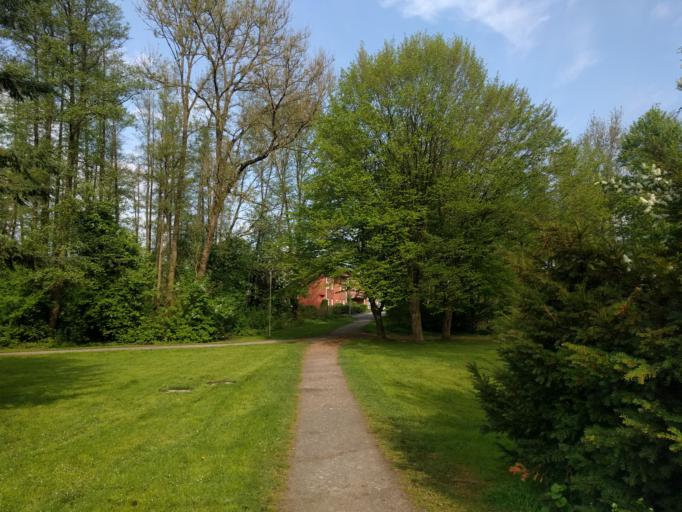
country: DE
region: North Rhine-Westphalia
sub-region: Regierungsbezirk Detmold
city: Bielefeld
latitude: 52.0510
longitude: 8.5156
